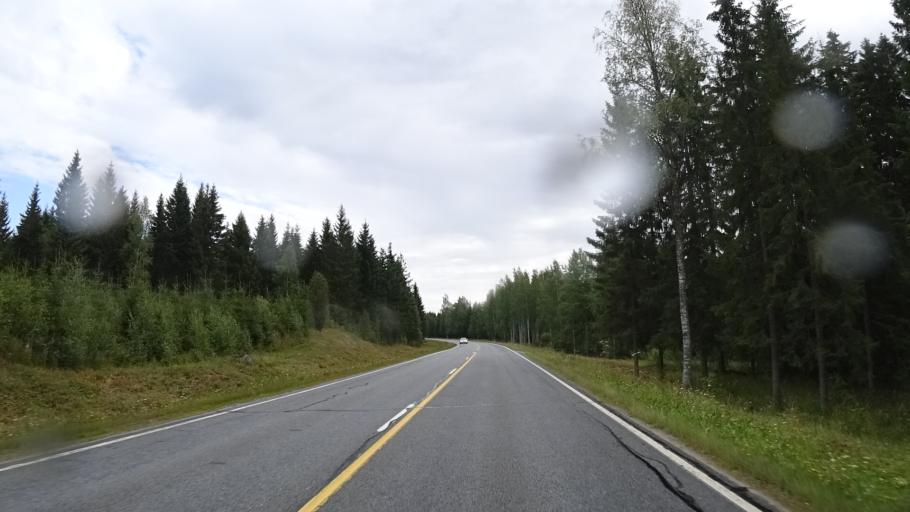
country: FI
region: North Karelia
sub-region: Keski-Karjala
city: Kesaelahti
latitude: 62.1101
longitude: 29.7481
